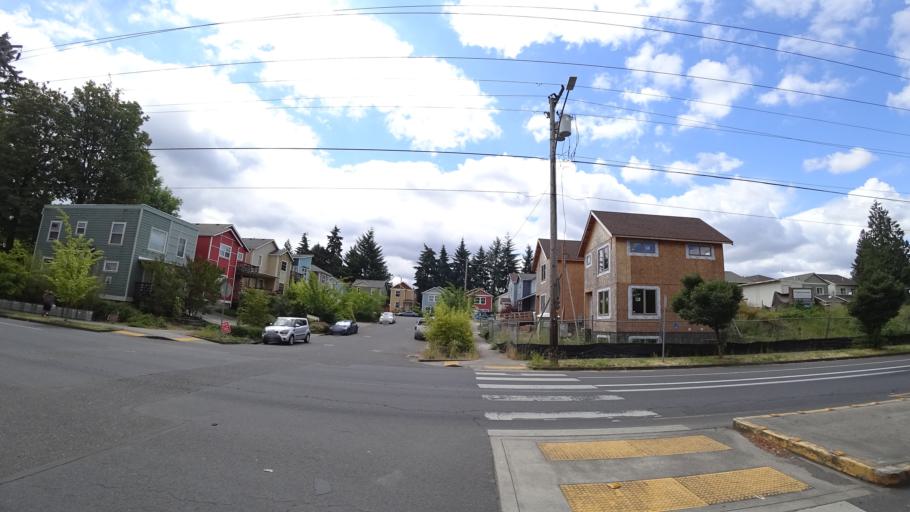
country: US
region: Oregon
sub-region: Multnomah County
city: Portland
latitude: 45.5628
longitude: -122.5978
